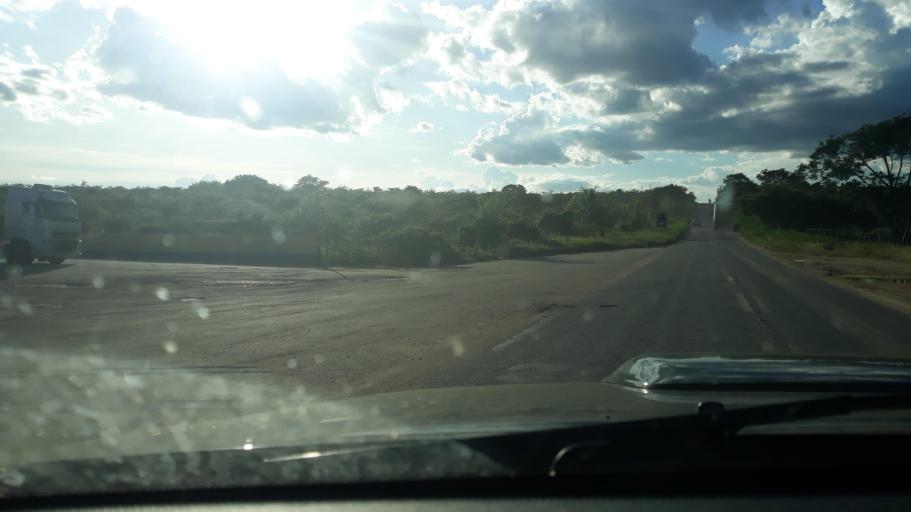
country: BR
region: Bahia
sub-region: Riacho De Santana
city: Riacho de Santana
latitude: -13.7646
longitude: -42.7278
